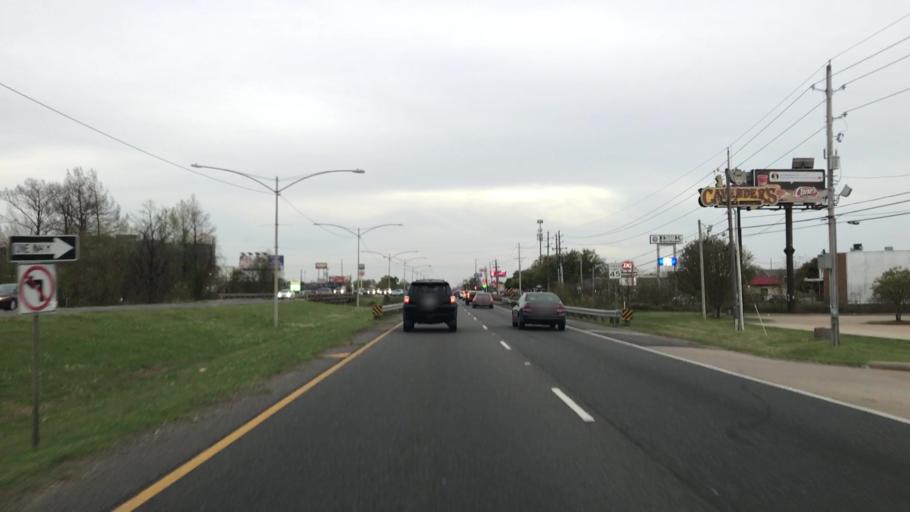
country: US
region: Louisiana
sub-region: Bossier Parish
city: Bossier City
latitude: 32.4359
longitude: -93.7144
